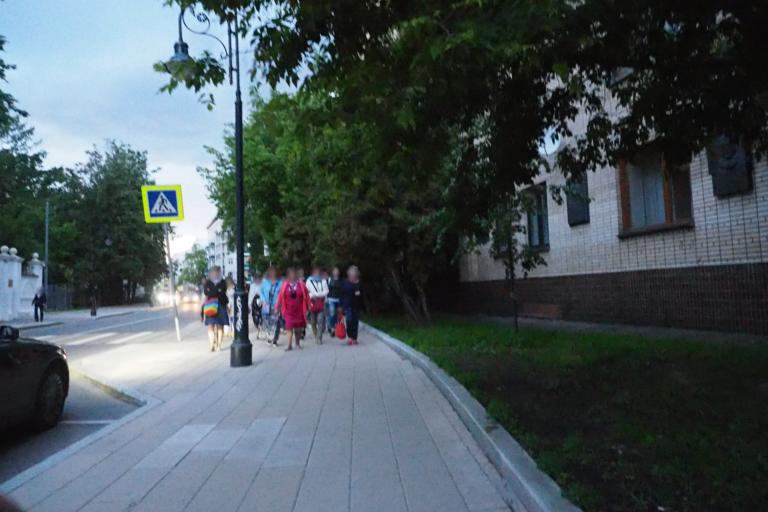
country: RU
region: Moscow
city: Moscow
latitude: 55.7608
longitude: 37.5933
